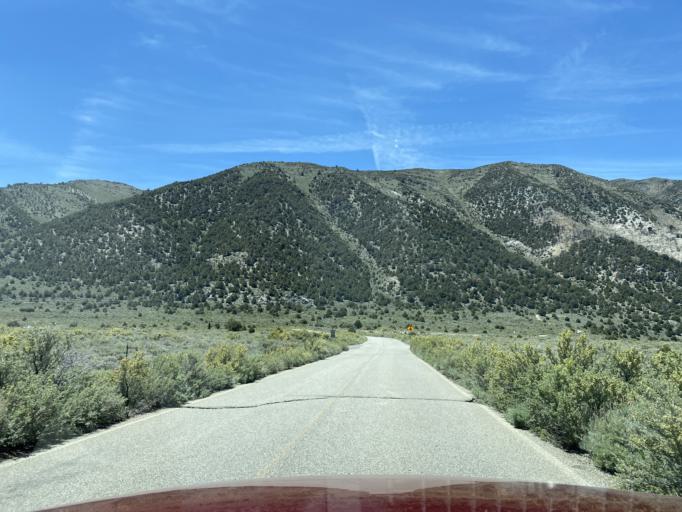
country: US
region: California
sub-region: Mono County
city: Bridgeport
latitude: 37.9648
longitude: -119.1213
